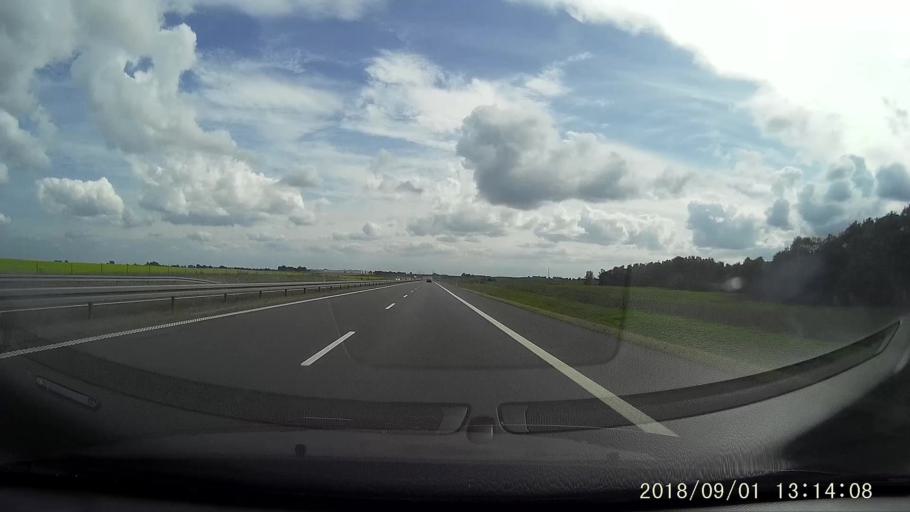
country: PL
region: West Pomeranian Voivodeship
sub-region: Powiat gryfinski
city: Gryfino
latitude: 53.2791
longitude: 14.6145
